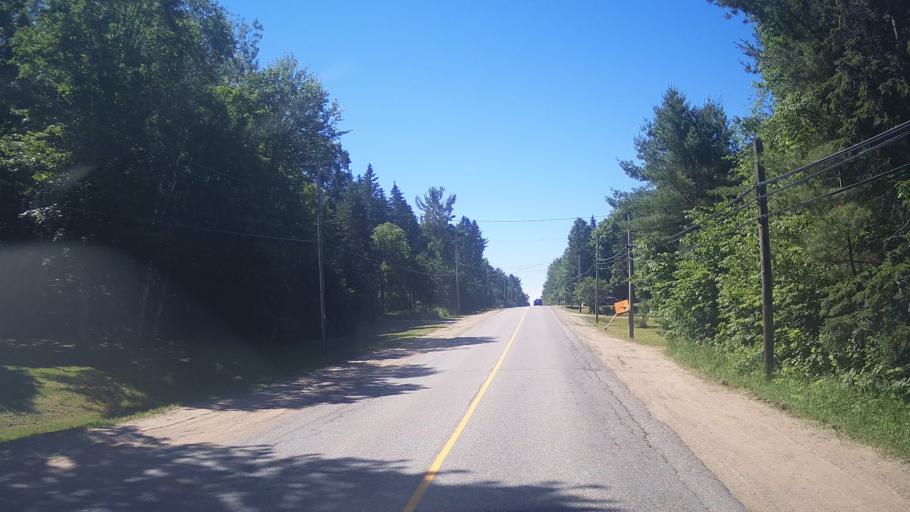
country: CA
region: Ontario
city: Huntsville
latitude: 45.3609
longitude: -79.2044
